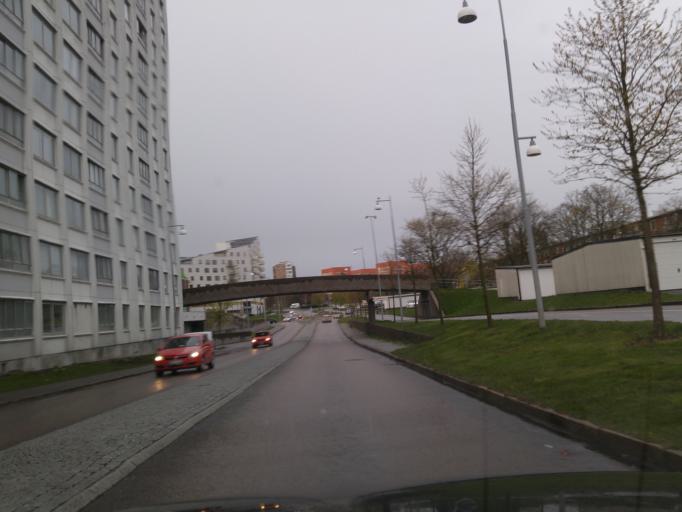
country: SE
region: Vaestra Goetaland
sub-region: Goteborg
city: Majorna
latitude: 57.6514
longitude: 11.9152
